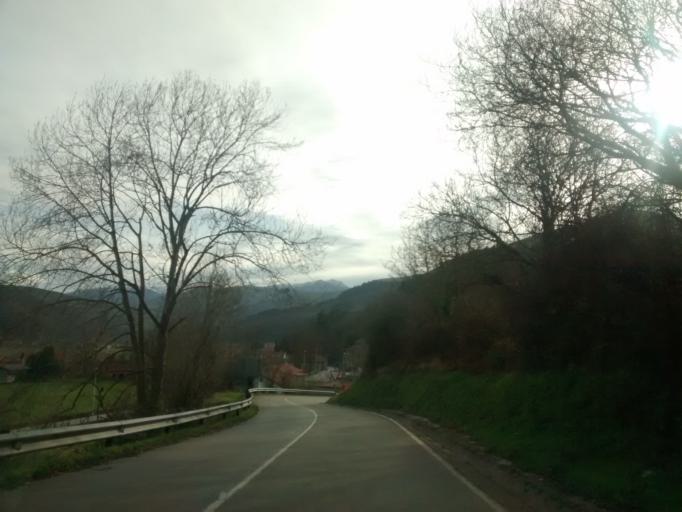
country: ES
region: Cantabria
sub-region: Provincia de Cantabria
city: Ruente
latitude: 43.2295
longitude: -4.3007
